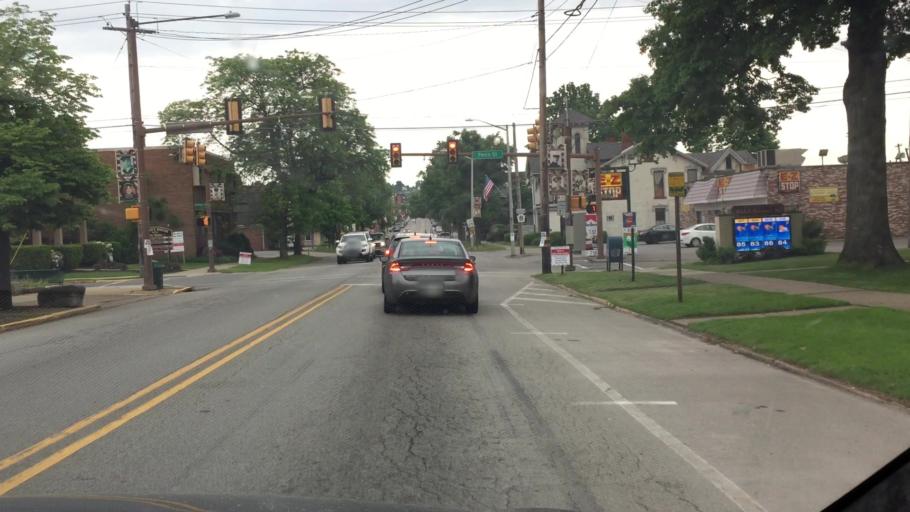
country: US
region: Pennsylvania
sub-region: Butler County
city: Butler
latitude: 40.8654
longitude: -79.8952
